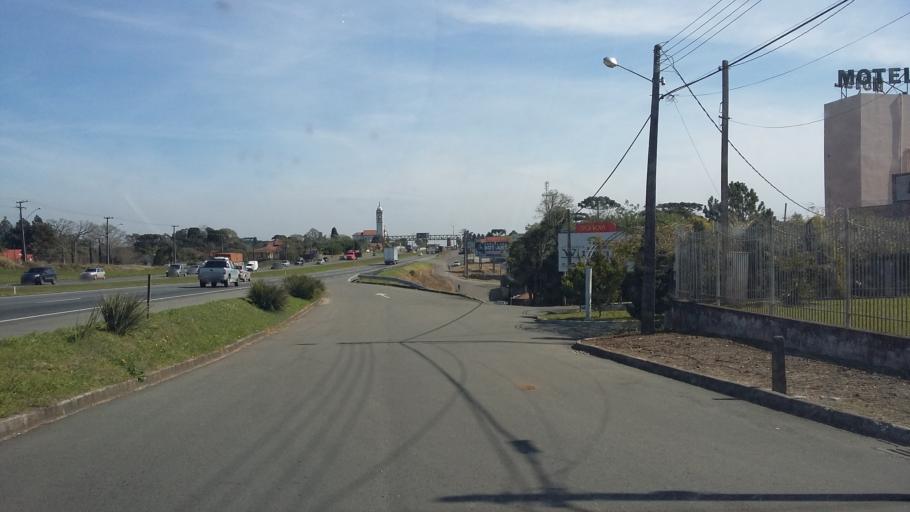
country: BR
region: Parana
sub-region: Campo Largo
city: Campo Largo
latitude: -25.4462
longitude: -49.4902
